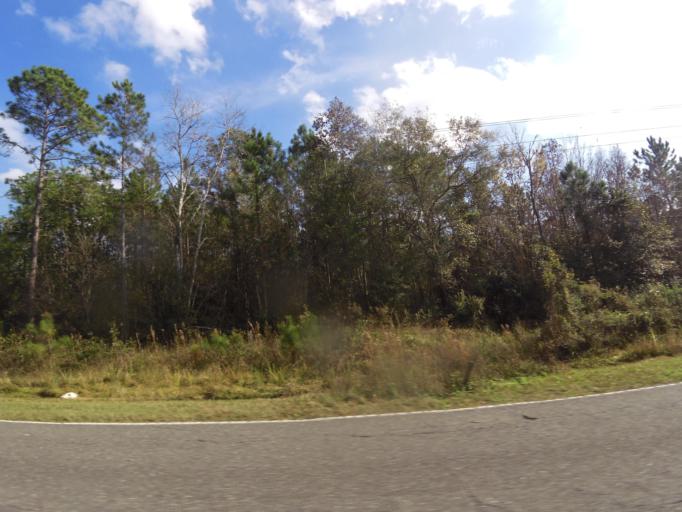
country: US
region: Florida
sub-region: Duval County
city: Baldwin
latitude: 30.1648
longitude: -81.9982
